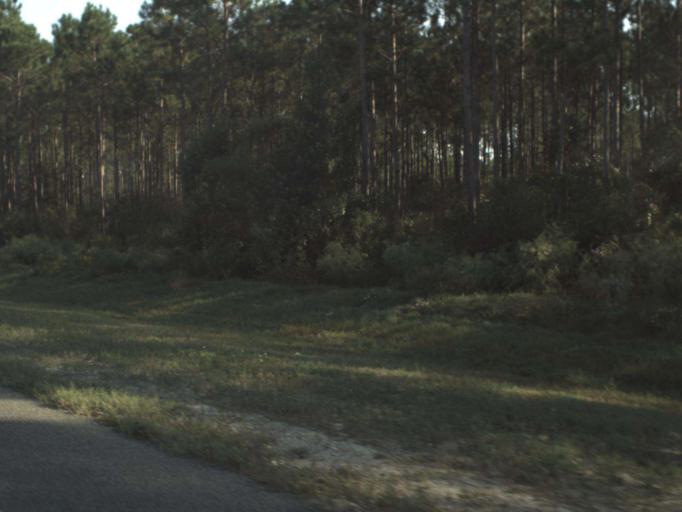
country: US
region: Florida
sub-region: Bay County
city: Laguna Beach
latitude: 30.3102
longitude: -85.8535
